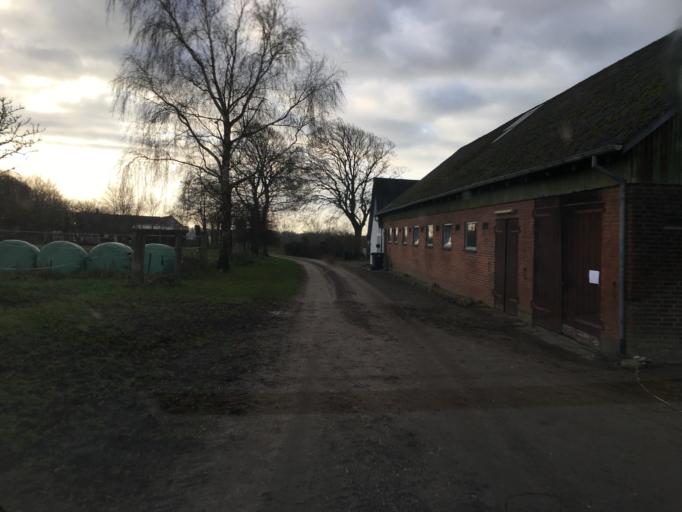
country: DK
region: South Denmark
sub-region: Tonder Kommune
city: Logumkloster
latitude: 55.1157
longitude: 8.8793
